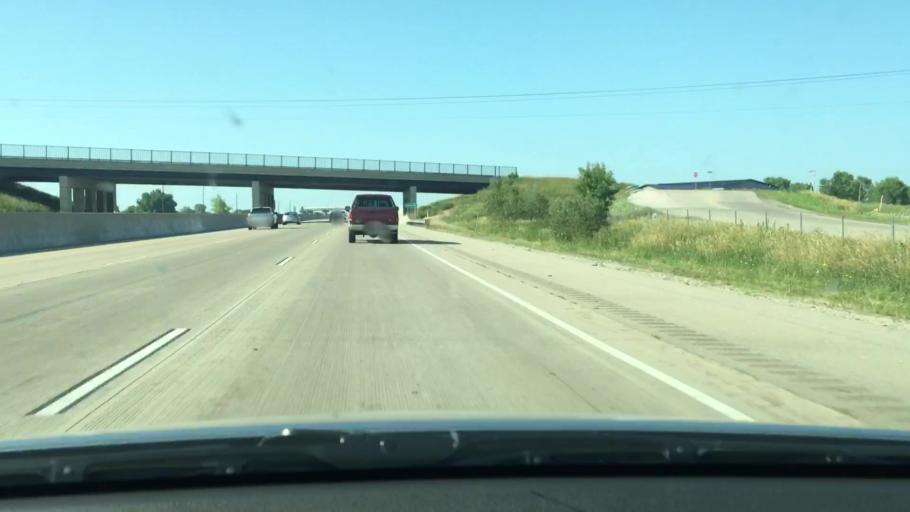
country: US
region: Wisconsin
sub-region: Winnebago County
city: Oshkosh
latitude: 44.0693
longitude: -88.5685
